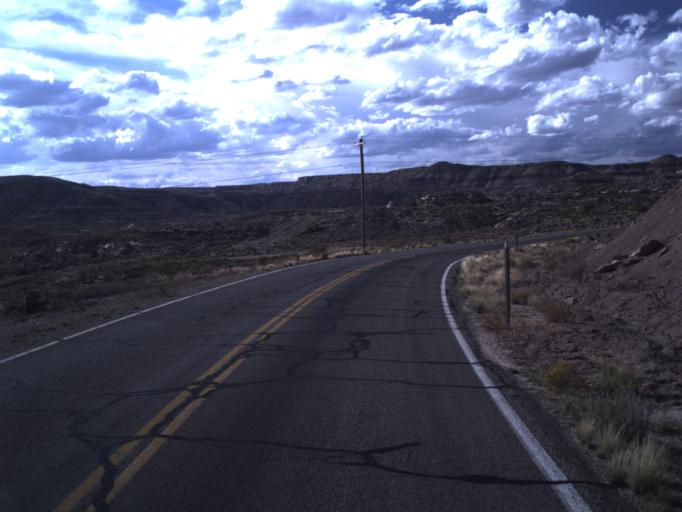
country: US
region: Utah
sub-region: San Juan County
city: Blanding
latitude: 37.3096
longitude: -109.3014
